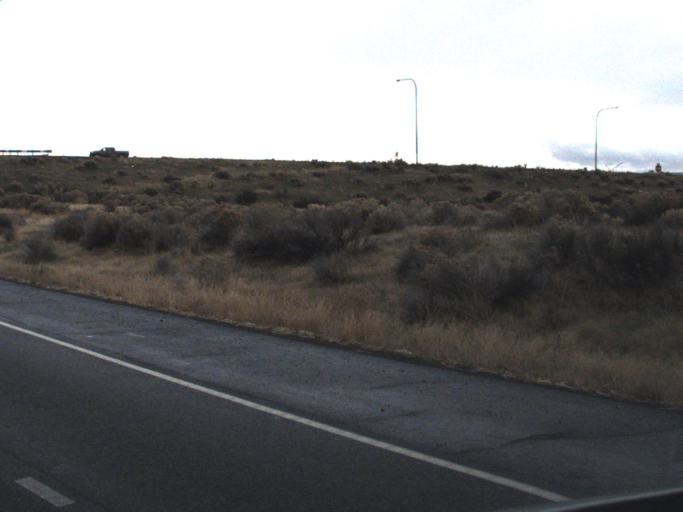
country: US
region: Washington
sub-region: Franklin County
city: Pasco
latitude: 46.2402
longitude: -119.0582
